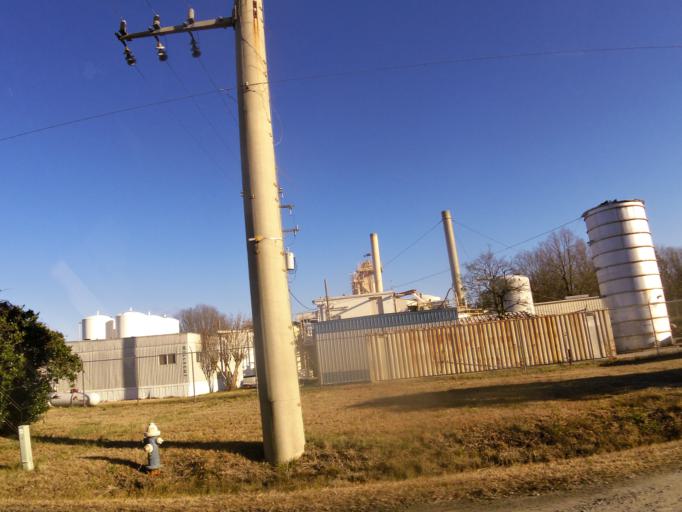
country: US
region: Virginia
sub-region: City of Hopewell
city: Hopewell
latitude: 37.2914
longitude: -77.2773
